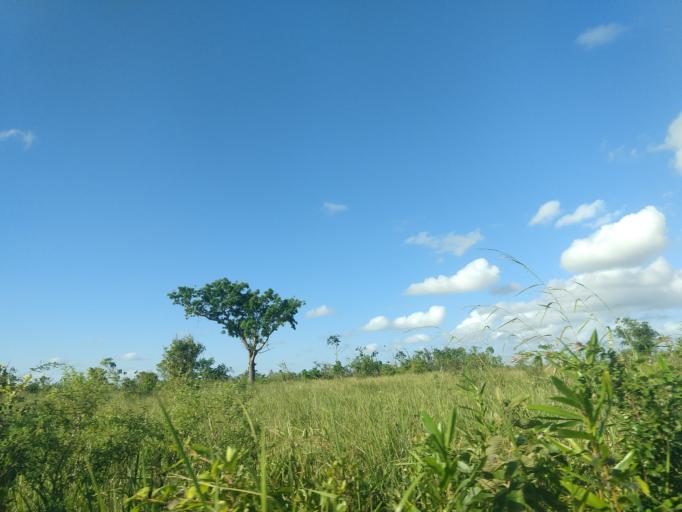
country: MZ
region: Sofala
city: Beira
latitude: -19.5973
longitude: 35.1341
